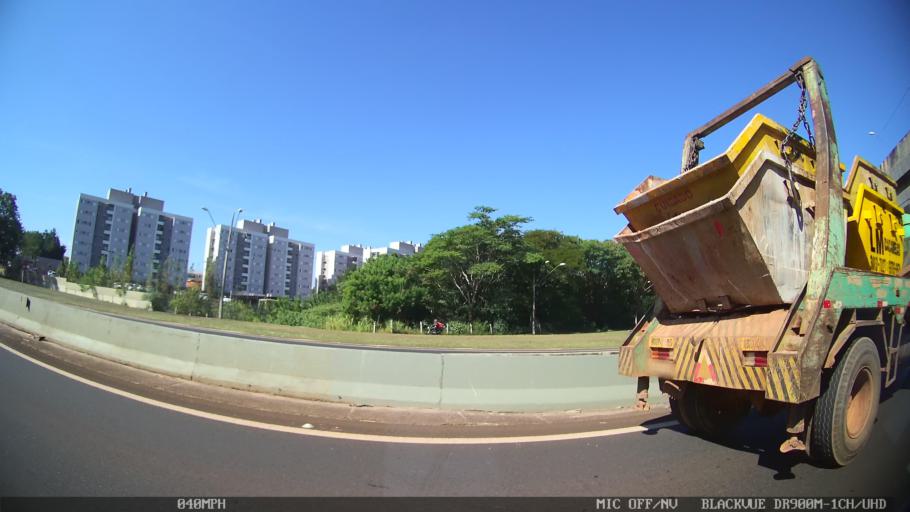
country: BR
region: Sao Paulo
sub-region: Ribeirao Preto
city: Ribeirao Preto
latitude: -21.2148
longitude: -47.7730
